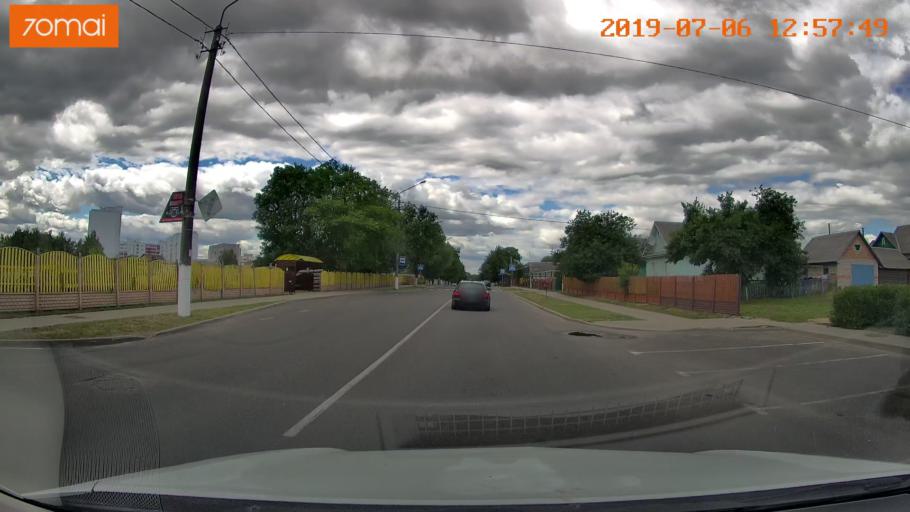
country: BY
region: Minsk
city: Dzyarzhynsk
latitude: 53.6868
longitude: 27.1495
